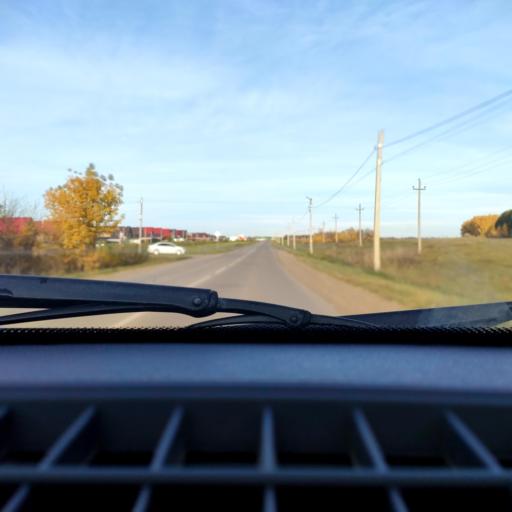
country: RU
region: Bashkortostan
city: Avdon
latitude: 54.6572
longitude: 55.7497
